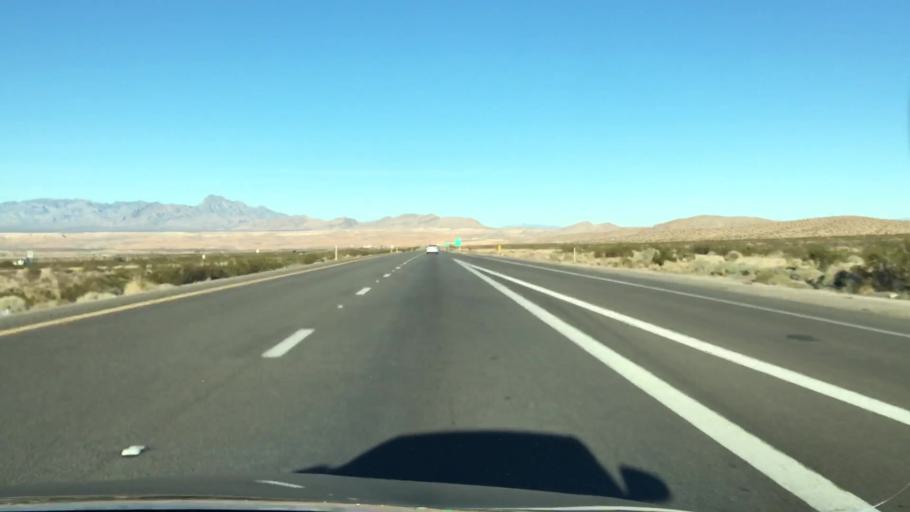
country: US
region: Nevada
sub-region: Clark County
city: Moapa Town
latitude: 36.6287
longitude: -114.6082
